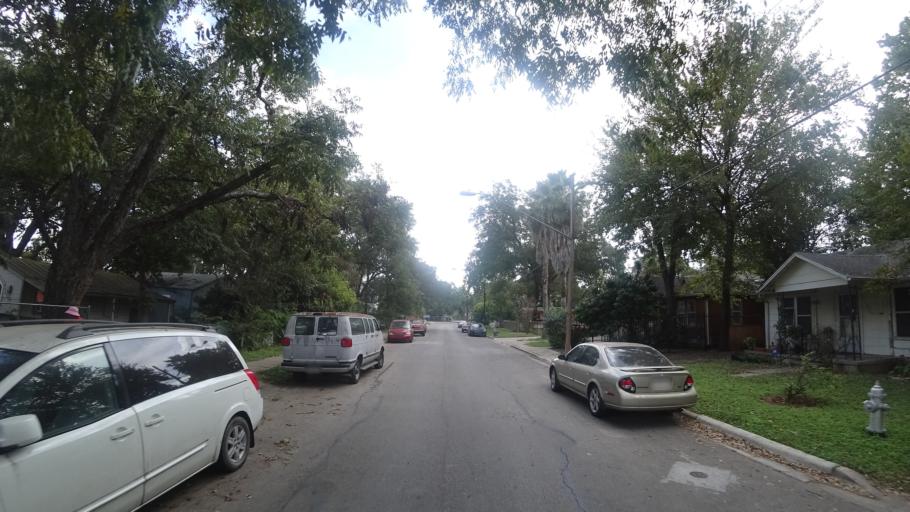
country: US
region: Texas
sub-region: Travis County
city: Austin
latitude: 30.2562
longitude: -97.7131
